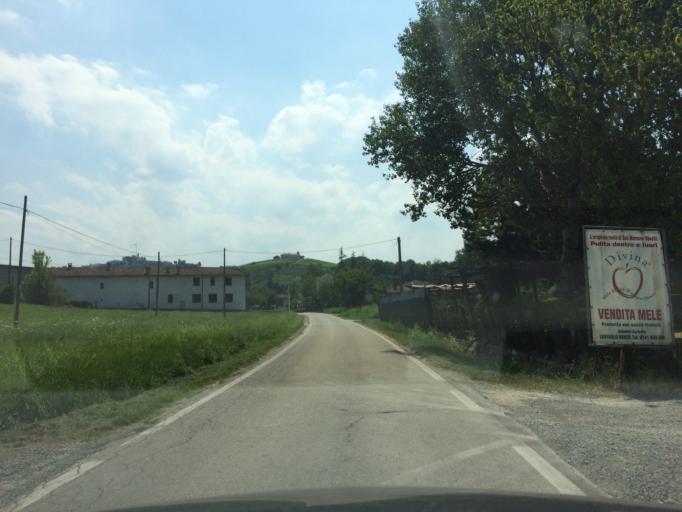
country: IT
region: Piedmont
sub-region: Provincia di Asti
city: San Marzano Oliveto
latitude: 44.7681
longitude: 8.3087
